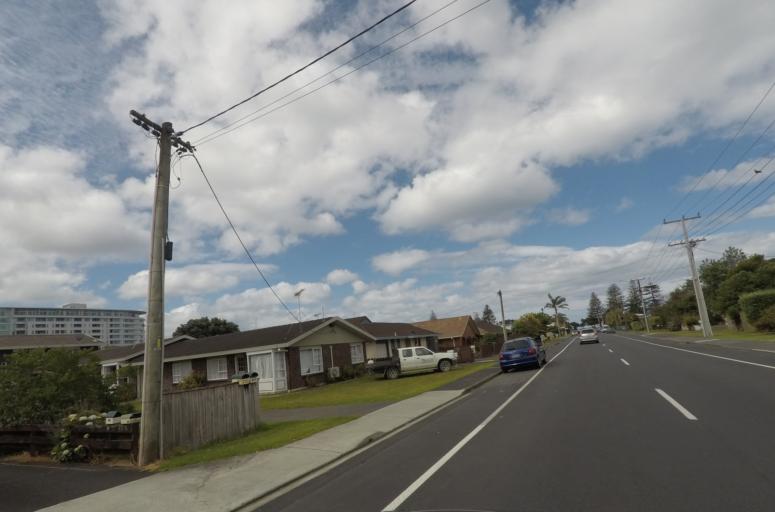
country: NZ
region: Auckland
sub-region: Auckland
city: Rothesay Bay
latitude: -36.5900
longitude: 174.6944
